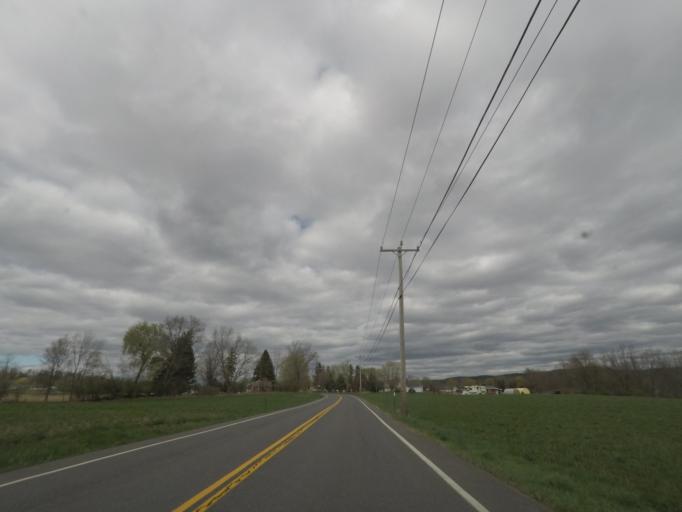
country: US
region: New York
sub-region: Columbia County
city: Philmont
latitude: 42.2856
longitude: -73.6511
